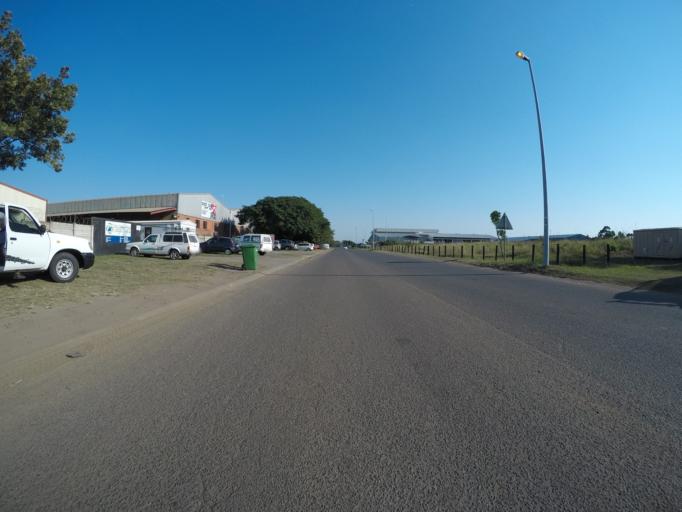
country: ZA
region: KwaZulu-Natal
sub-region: uThungulu District Municipality
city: Richards Bay
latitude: -28.7499
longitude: 32.0243
